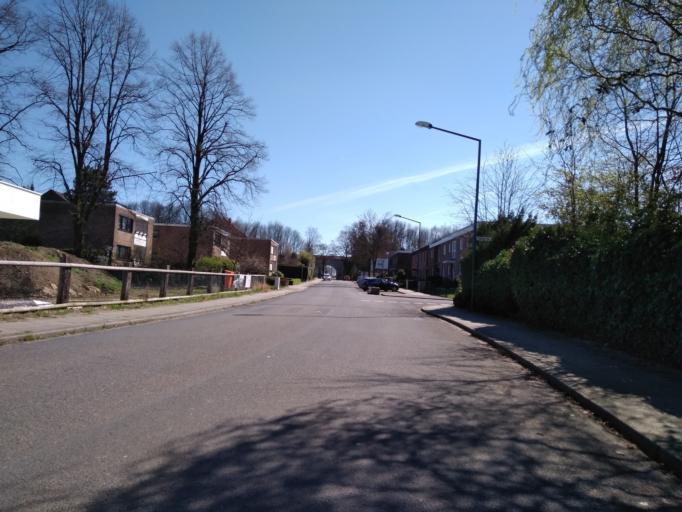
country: DE
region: North Rhine-Westphalia
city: Herten
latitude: 51.6115
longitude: 7.1090
